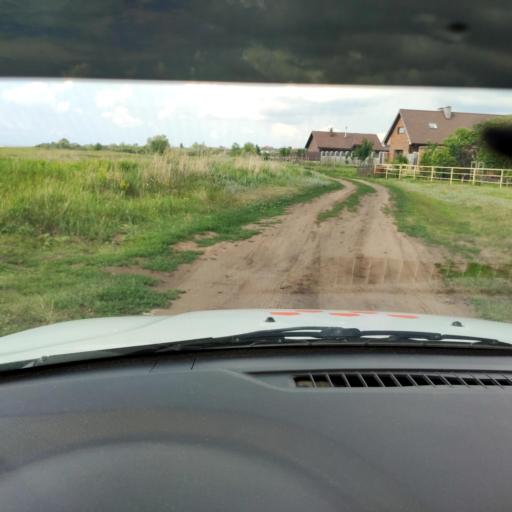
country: RU
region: Samara
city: Podstepki
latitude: 53.6111
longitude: 49.0299
